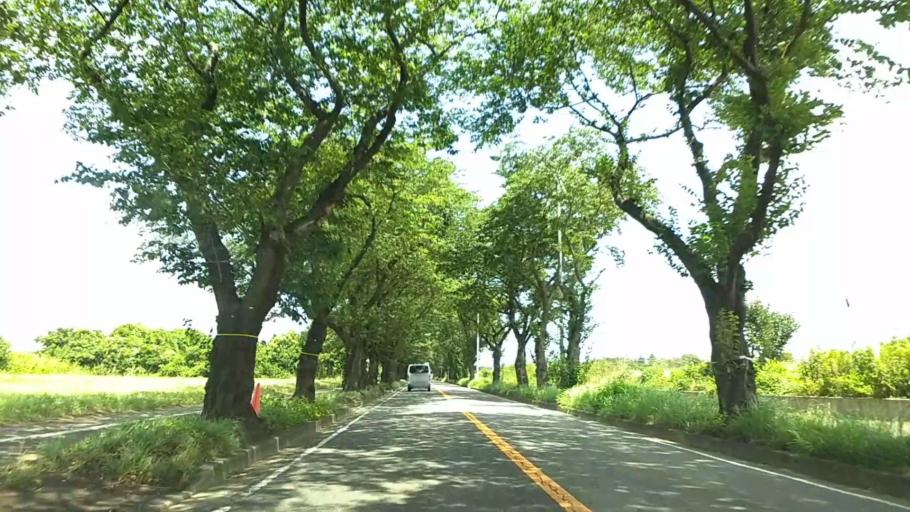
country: JP
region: Kanagawa
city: Minami-rinkan
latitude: 35.4912
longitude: 139.4802
